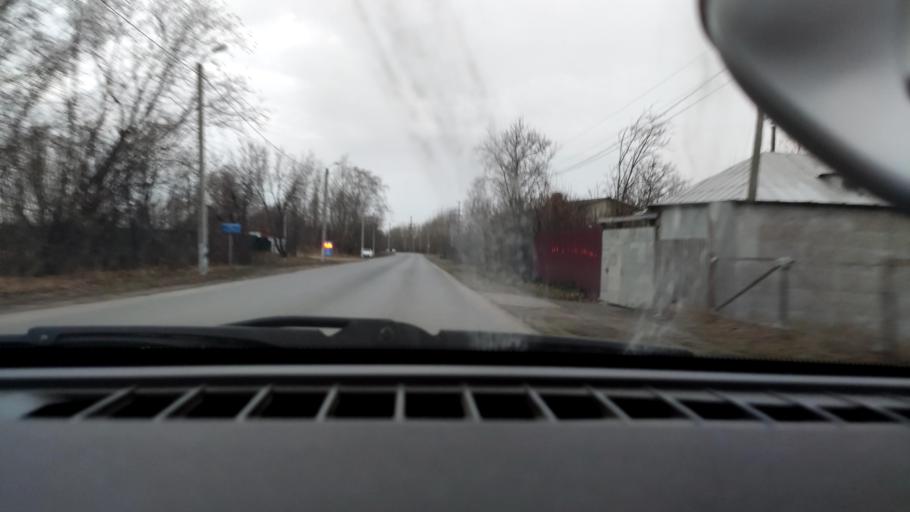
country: RU
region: Perm
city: Kondratovo
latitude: 57.9403
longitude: 56.1550
